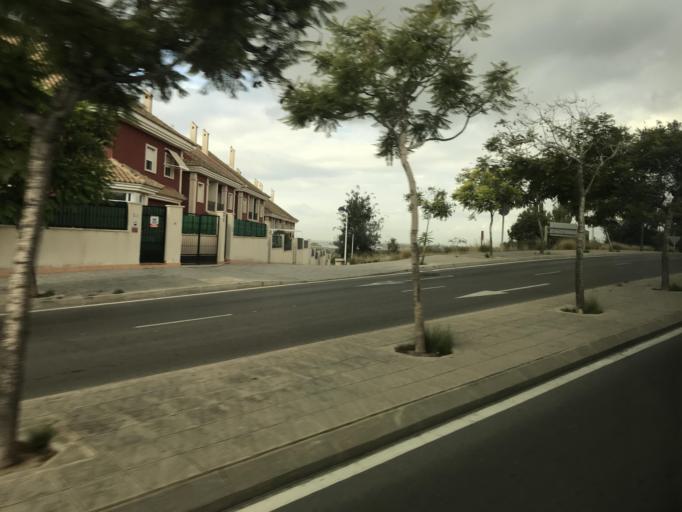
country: ES
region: Valencia
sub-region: Provincia de Alicante
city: Santa Pola
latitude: 38.2012
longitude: -0.5621
